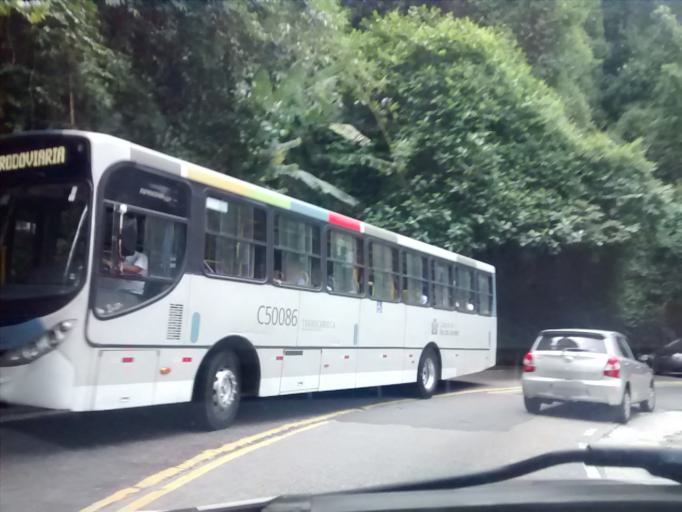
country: BR
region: Rio de Janeiro
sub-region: Rio De Janeiro
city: Rio de Janeiro
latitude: -22.9684
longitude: -43.2789
